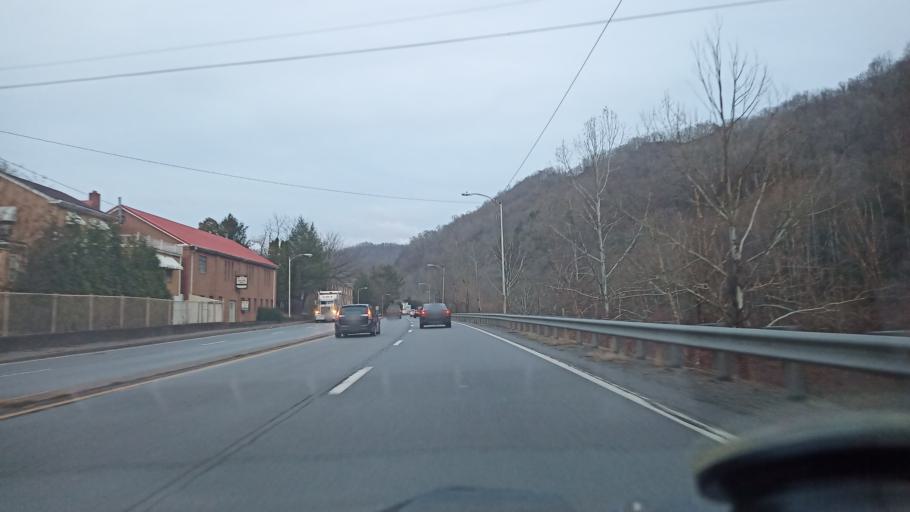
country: US
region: West Virginia
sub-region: Logan County
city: Logan
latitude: 37.8444
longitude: -81.9860
